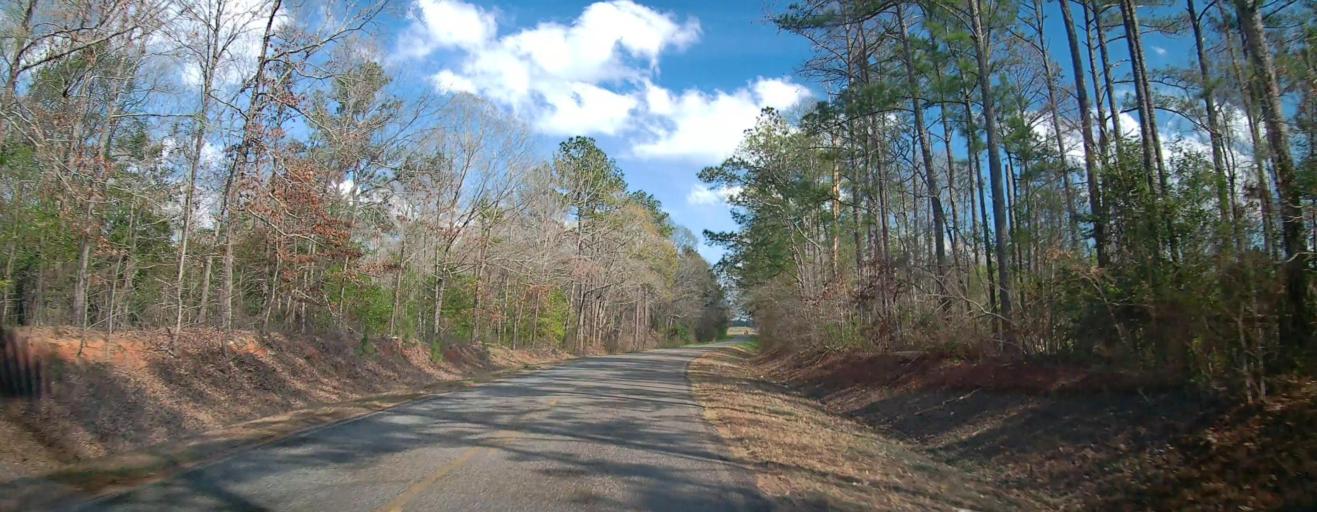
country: US
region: Georgia
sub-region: Wilkinson County
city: Irwinton
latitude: 32.6389
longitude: -83.1602
